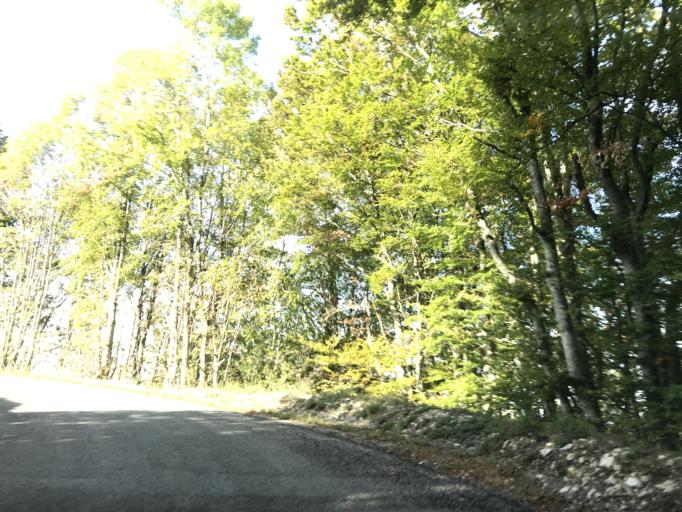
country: FR
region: Rhone-Alpes
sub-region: Departement de la Savoie
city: Novalaise
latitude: 45.6378
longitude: 5.7993
